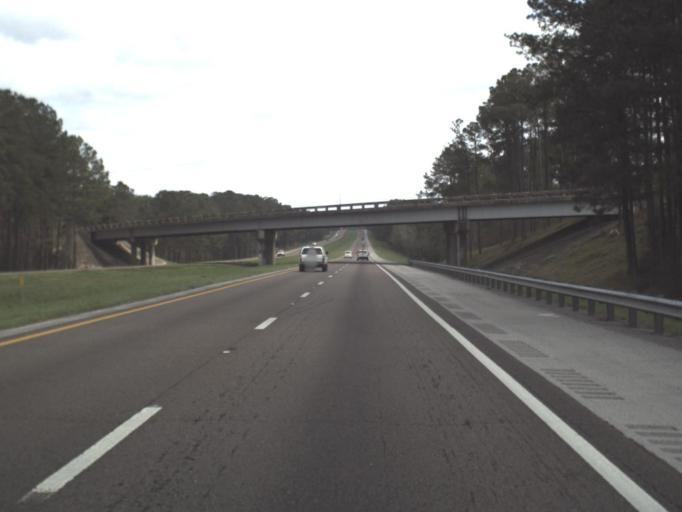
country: US
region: Florida
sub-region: Walton County
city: DeFuniak Springs
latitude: 30.7073
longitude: -86.1648
